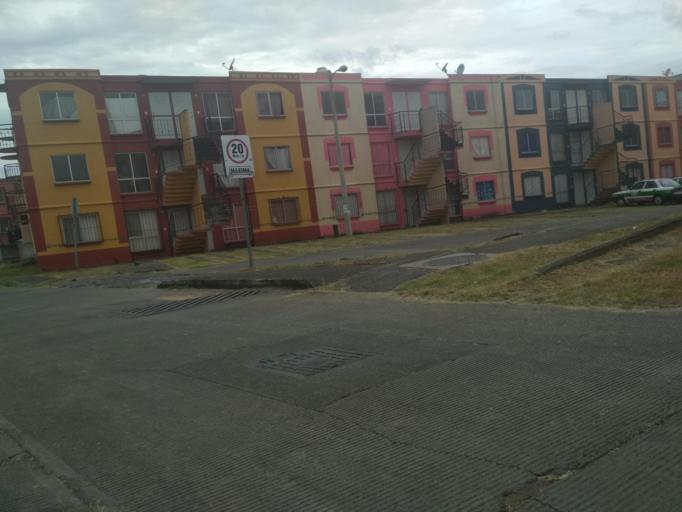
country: MX
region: Veracruz
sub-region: Coatepec
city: Las Lomas
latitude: 19.4175
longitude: -96.9283
